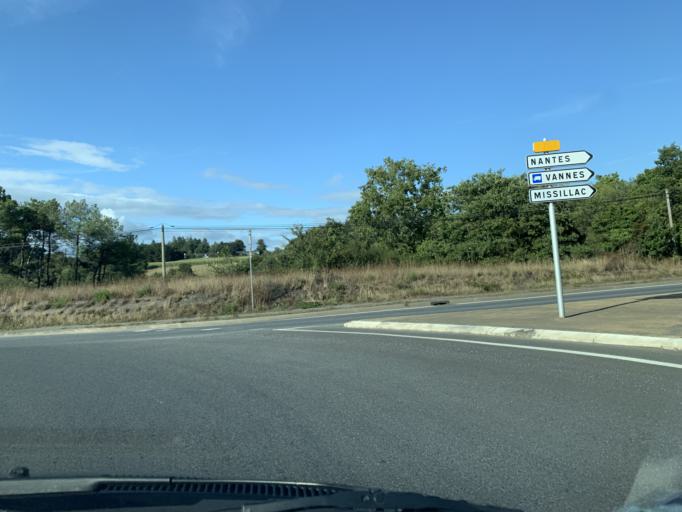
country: FR
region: Brittany
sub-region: Departement du Morbihan
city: Nivillac
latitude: 47.5115
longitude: -2.2853
